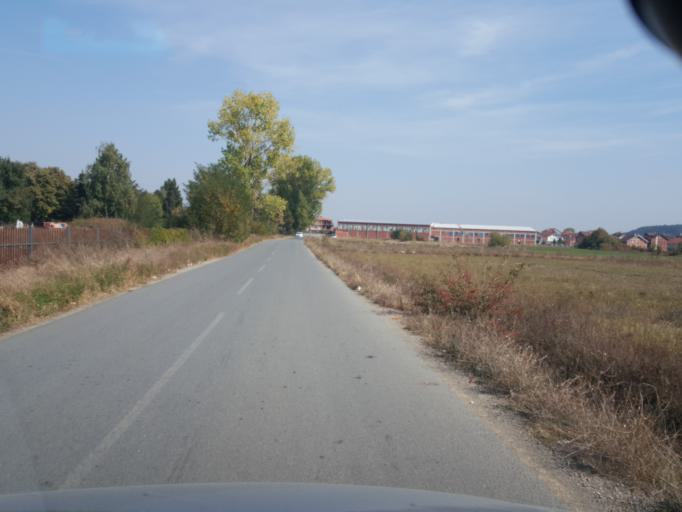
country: XK
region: Gjakova
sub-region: Komuna e Gjakoves
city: Gjakove
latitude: 42.3699
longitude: 20.4058
